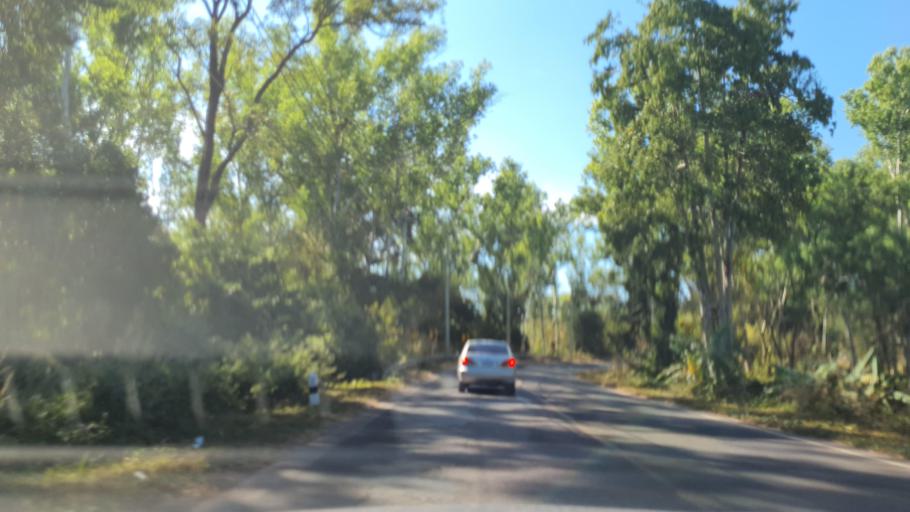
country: TH
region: Kalasin
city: Khao Wong
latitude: 16.7640
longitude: 104.1419
